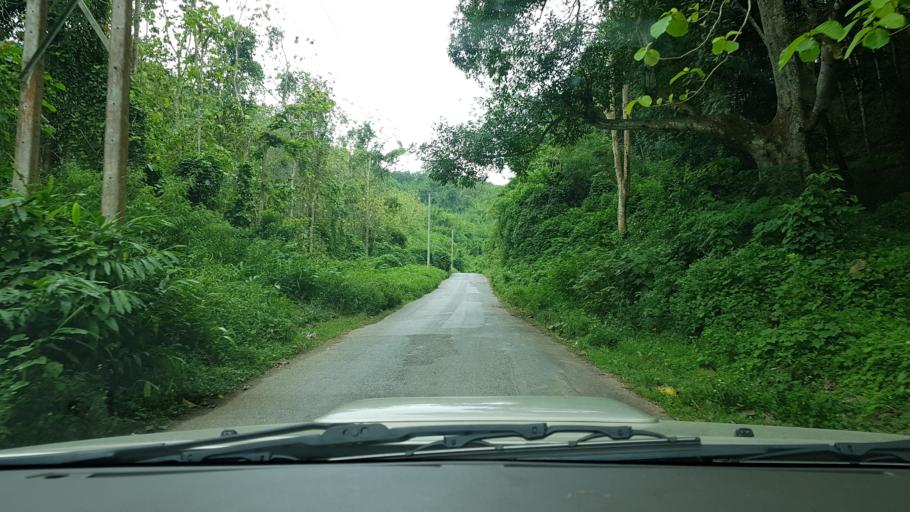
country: LA
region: Phongsali
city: Khoa
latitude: 21.0811
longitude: 102.3722
